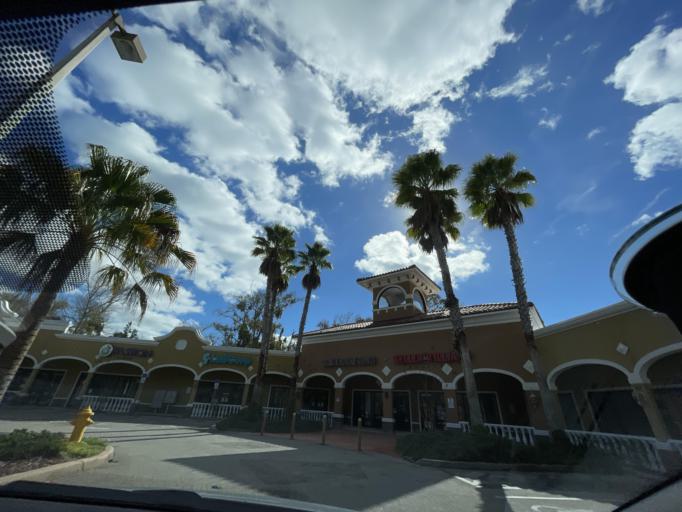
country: US
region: Florida
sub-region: Volusia County
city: Port Orange
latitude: 29.1420
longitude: -81.0144
